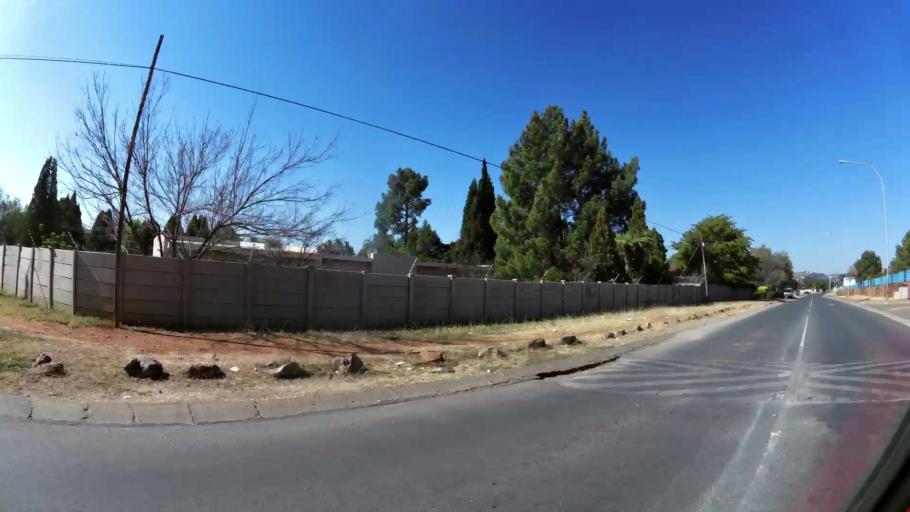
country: ZA
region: Gauteng
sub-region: City of Johannesburg Metropolitan Municipality
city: Roodepoort
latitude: -26.1206
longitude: 27.9210
